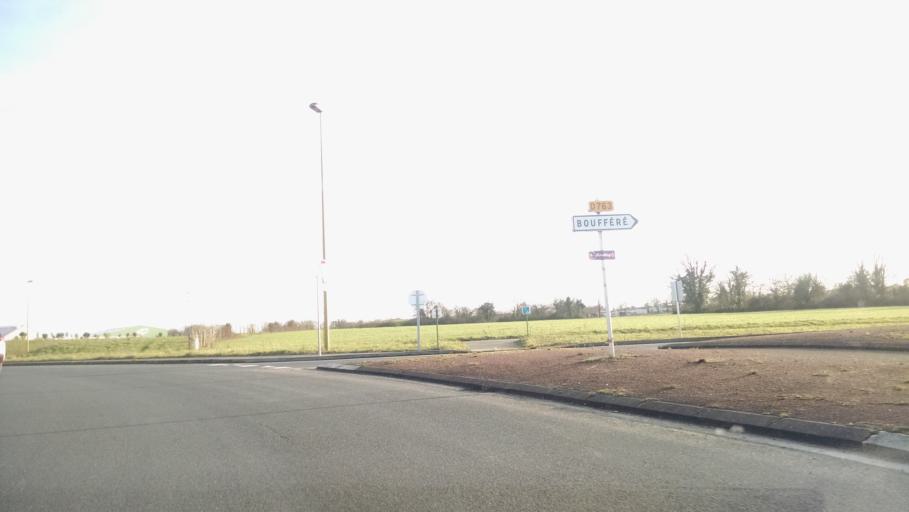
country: FR
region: Pays de la Loire
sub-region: Departement de la Vendee
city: Bouffere
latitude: 46.9692
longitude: -1.3303
